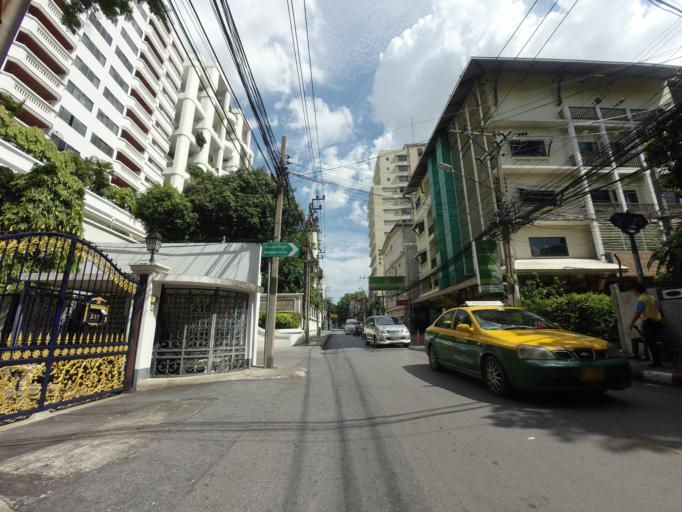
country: TH
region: Bangkok
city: Khlong Toei
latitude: 13.7358
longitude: 100.5531
